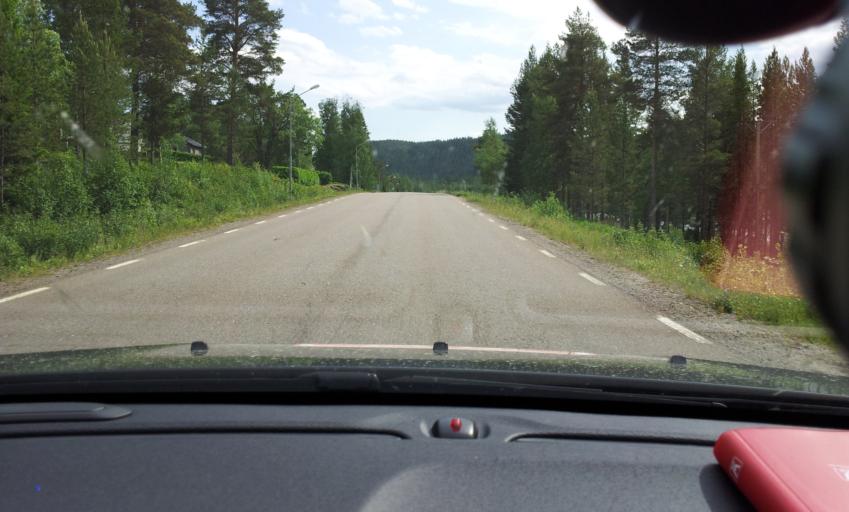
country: SE
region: Jaemtland
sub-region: Bergs Kommun
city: Hoverberg
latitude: 62.6632
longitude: 14.7464
